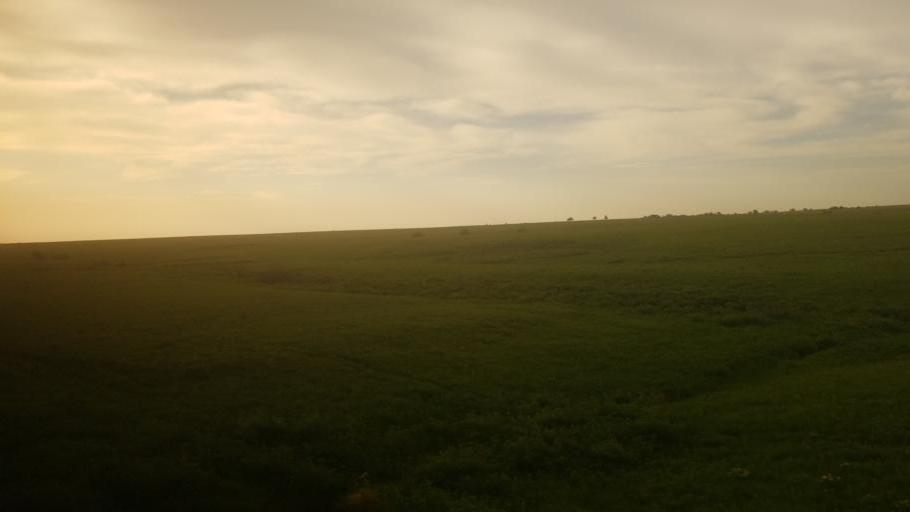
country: US
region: Kansas
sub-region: Lyon County
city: Emporia
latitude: 38.5000
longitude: -96.0087
